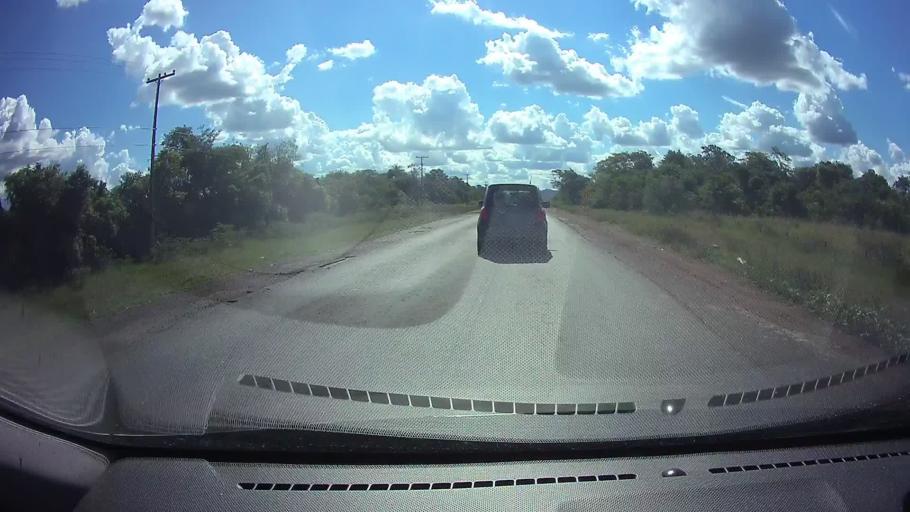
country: PY
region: Paraguari
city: La Colmena
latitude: -25.7516
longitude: -56.7849
